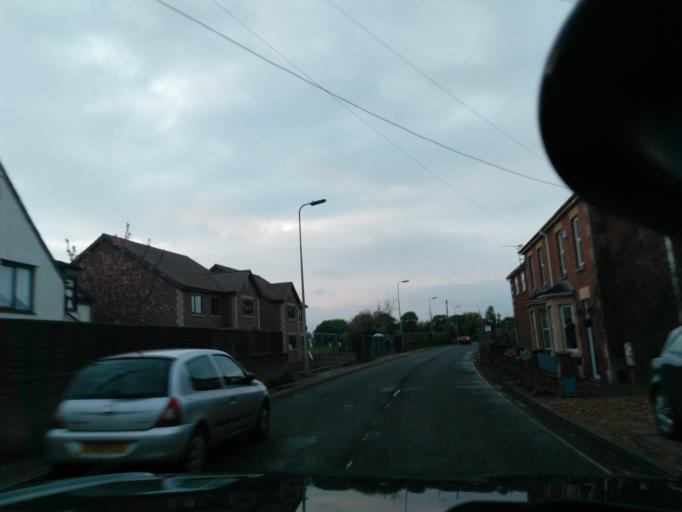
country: GB
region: England
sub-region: Wiltshire
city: Melksham
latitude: 51.3618
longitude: -2.1434
